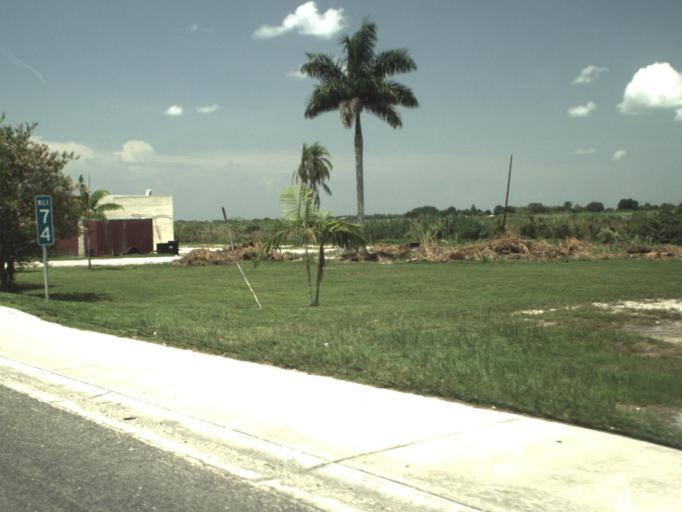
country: US
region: Florida
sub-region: Palm Beach County
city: South Bay
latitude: 26.6708
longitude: -80.7195
